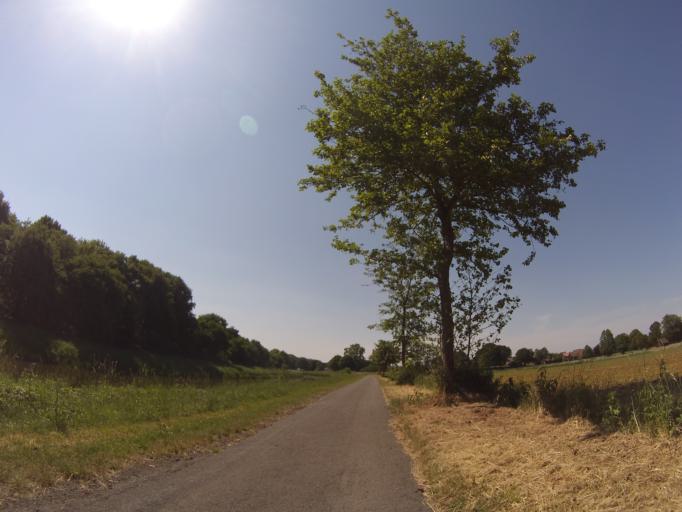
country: DE
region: Lower Saxony
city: Emlichheim
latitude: 52.6018
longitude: 6.8422
